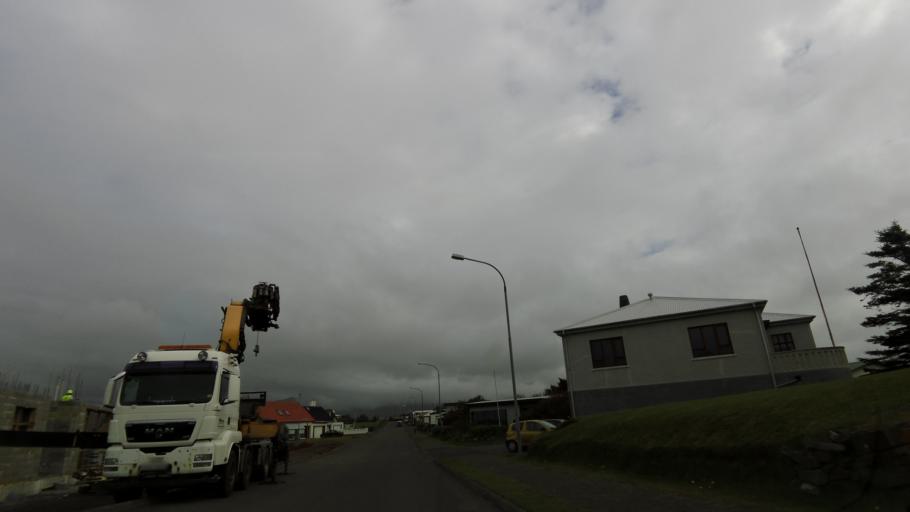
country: IS
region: East
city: Hoefn
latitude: 64.2551
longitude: -15.2141
